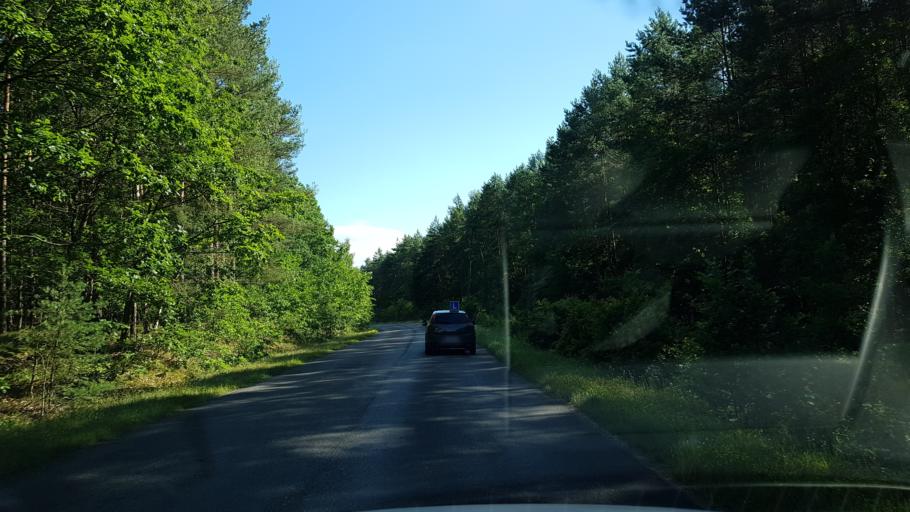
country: PL
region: West Pomeranian Voivodeship
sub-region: Powiat goleniowski
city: Stepnica
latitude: 53.7094
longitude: 14.6673
